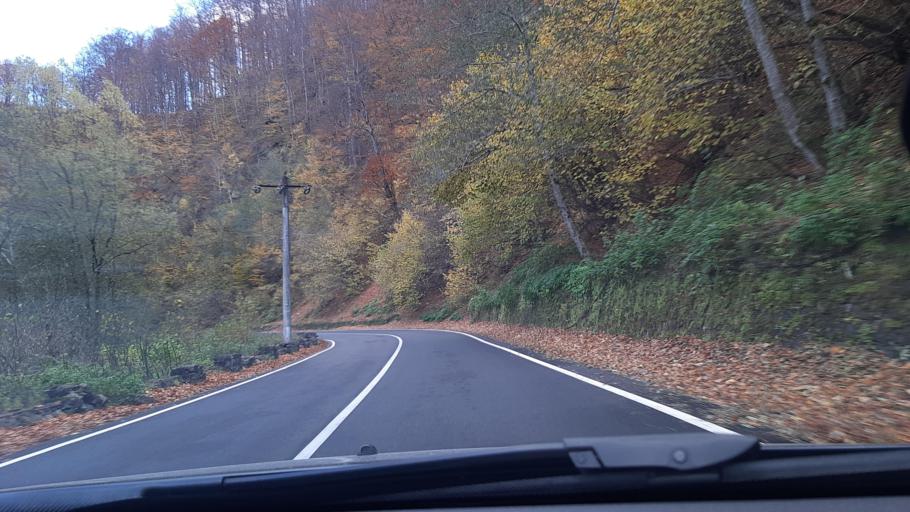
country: RO
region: Valcea
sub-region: Comuna Voineasa
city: Voineasa
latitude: 45.4048
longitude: 23.9916
